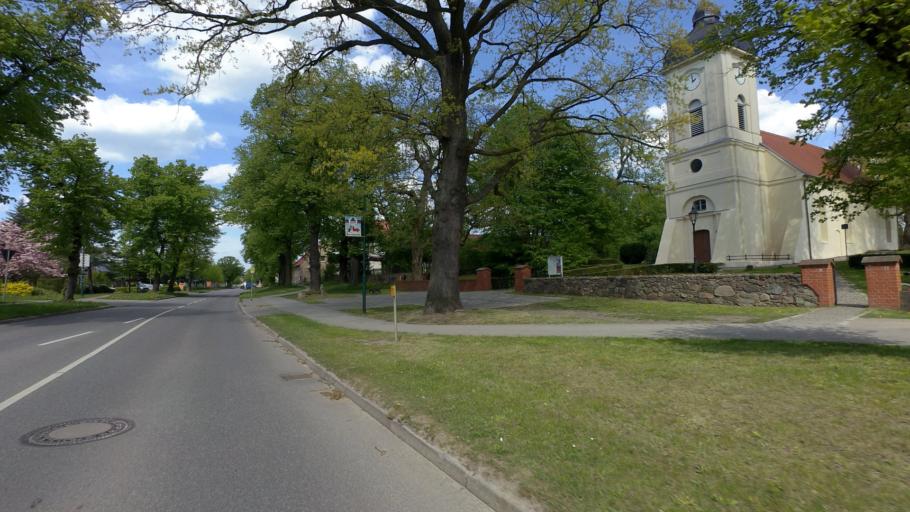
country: DE
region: Brandenburg
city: Wandlitz
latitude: 52.7921
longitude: 13.4799
